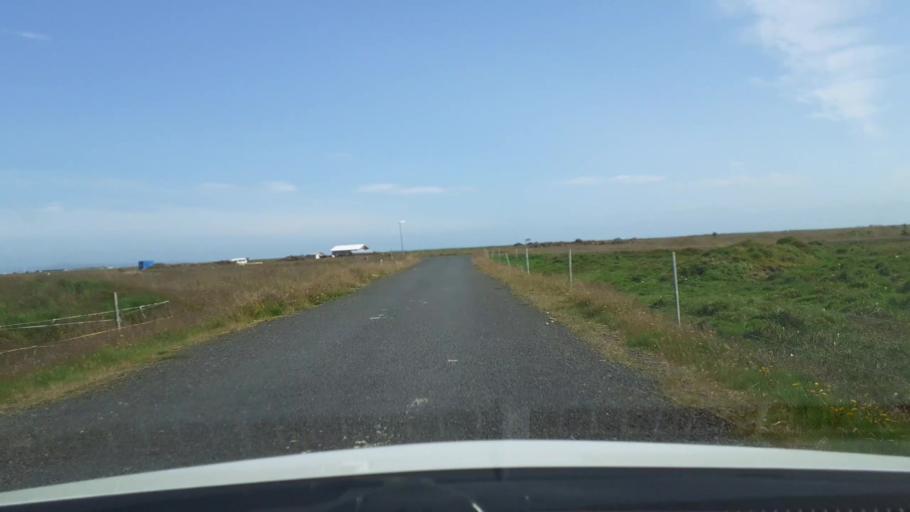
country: IS
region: South
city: Selfoss
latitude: 63.8890
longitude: -21.0886
